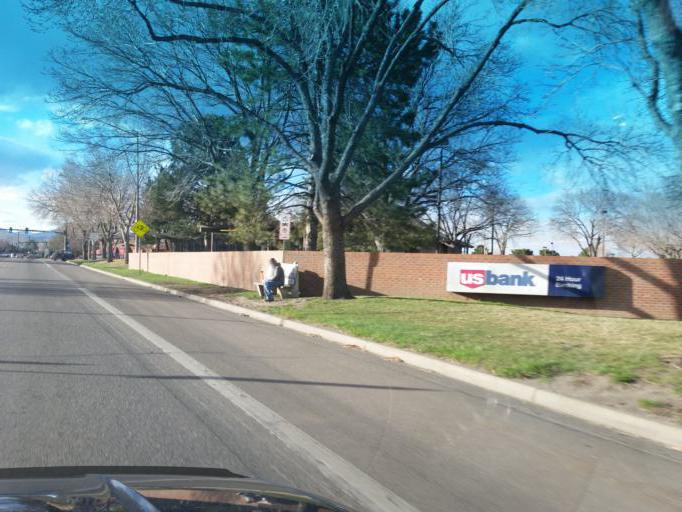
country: US
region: Colorado
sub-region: Larimer County
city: Loveland
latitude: 40.4205
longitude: -105.0747
